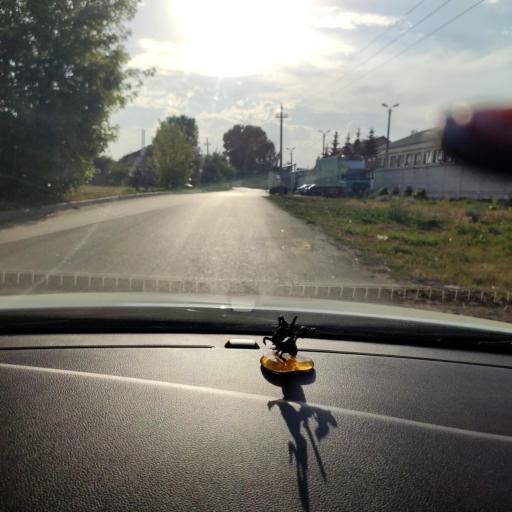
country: RU
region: Tatarstan
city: Staroye Arakchino
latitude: 55.8148
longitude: 48.9099
